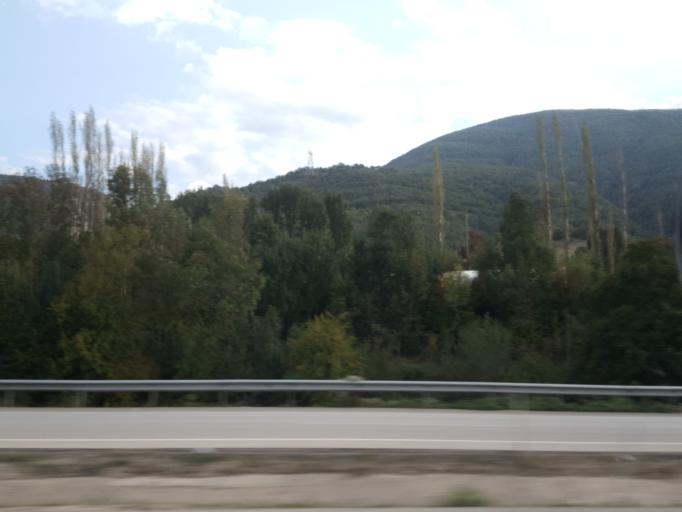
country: TR
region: Tokat
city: Bereketli
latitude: 40.4183
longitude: 37.1996
